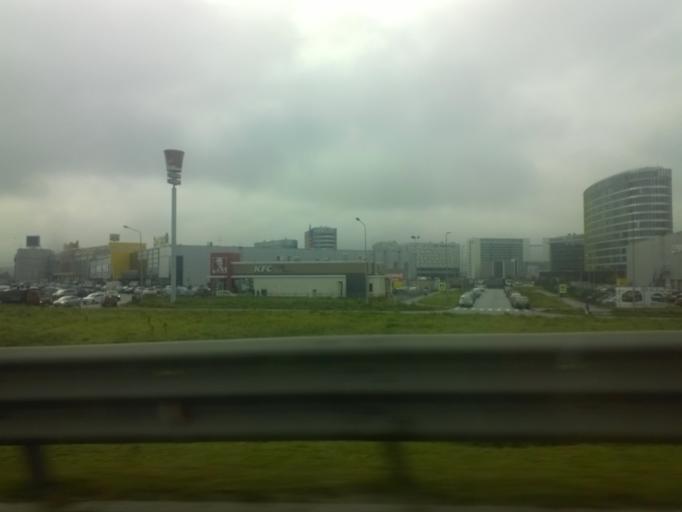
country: RU
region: St.-Petersburg
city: Kupchino
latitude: 59.8098
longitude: 30.3217
